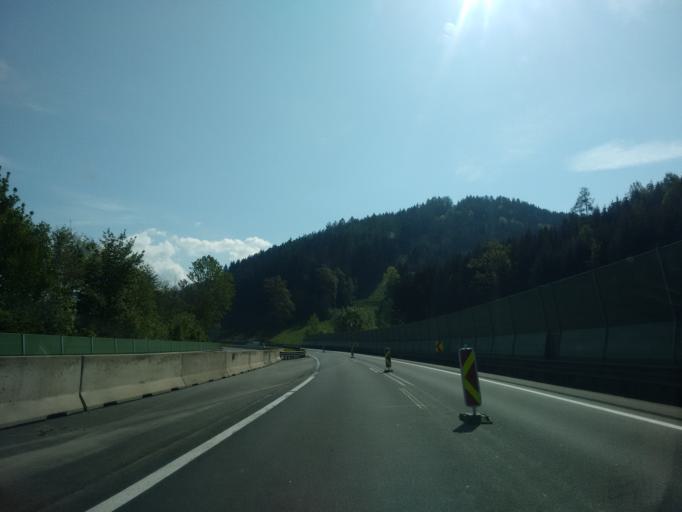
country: AT
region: Styria
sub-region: Politischer Bezirk Bruck-Muerzzuschlag
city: Oberaich
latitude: 47.3975
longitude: 15.2351
